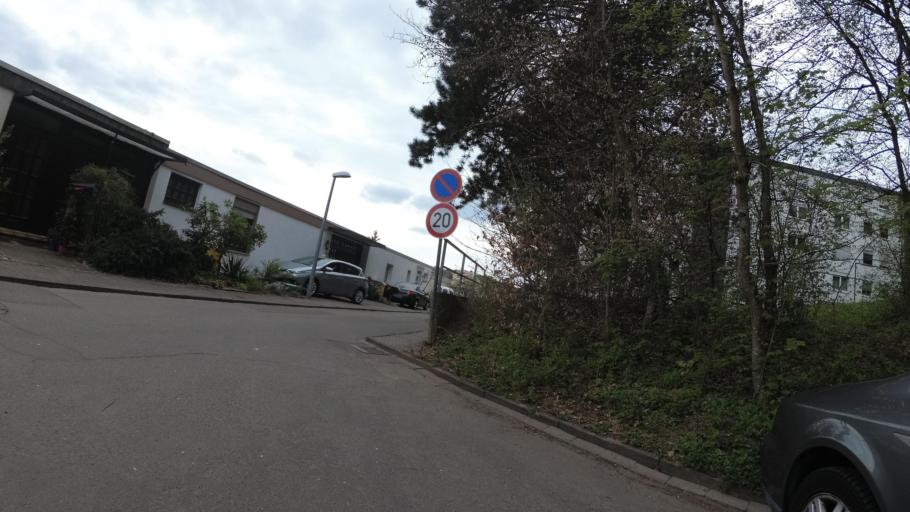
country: DE
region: Rheinland-Pfalz
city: Contwig
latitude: 49.2569
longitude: 7.4047
